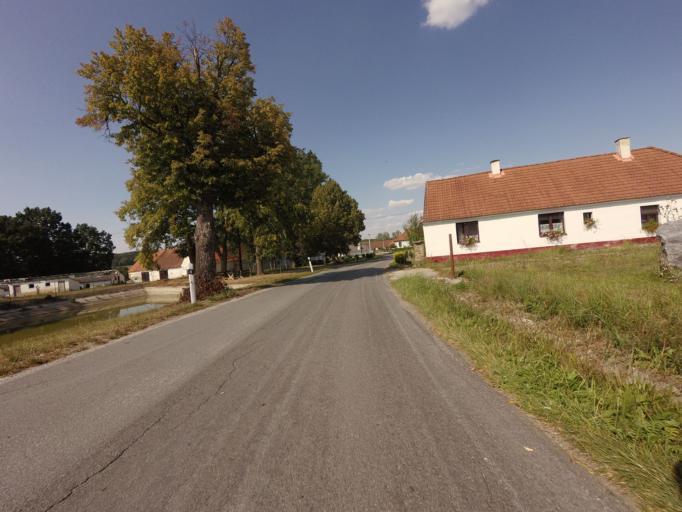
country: CZ
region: Jihocesky
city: Tyn nad Vltavou
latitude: 49.1480
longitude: 14.4446
